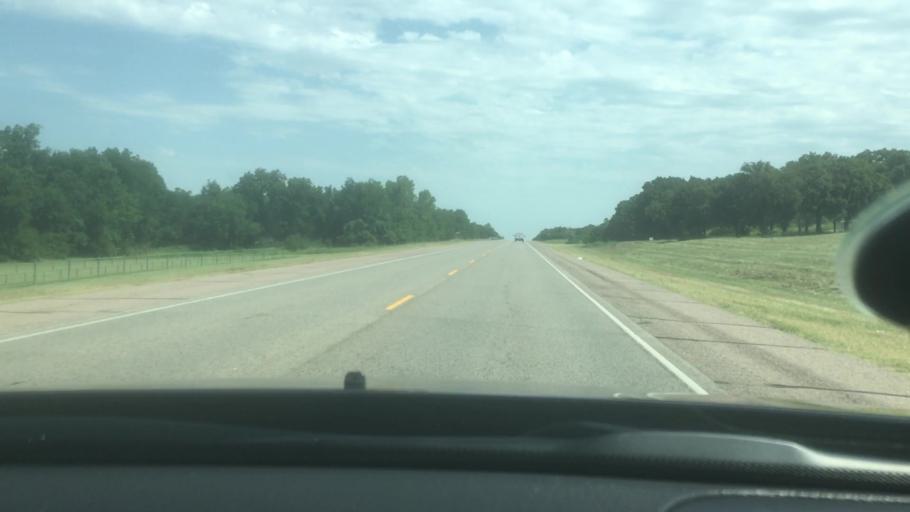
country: US
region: Oklahoma
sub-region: Seminole County
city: Konawa
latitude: 35.0048
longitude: -96.9314
